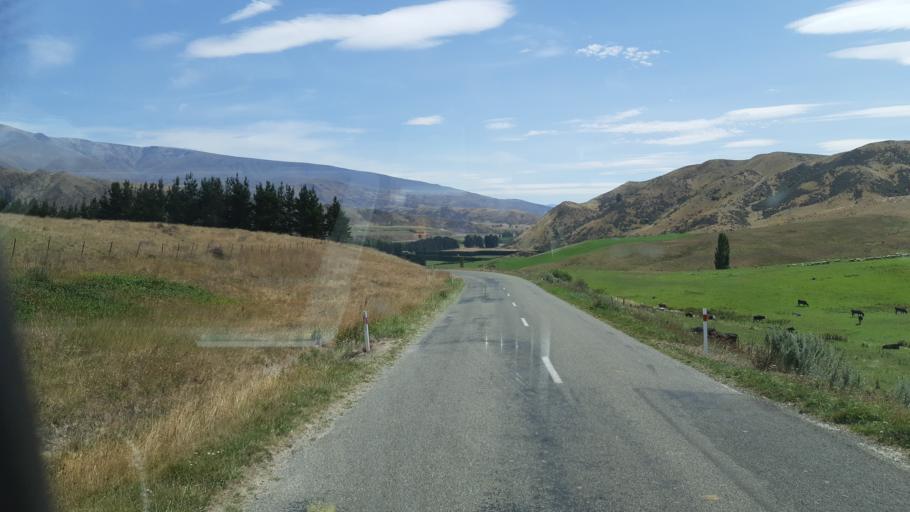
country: NZ
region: Otago
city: Oamaru
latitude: -44.7153
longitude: 170.4825
